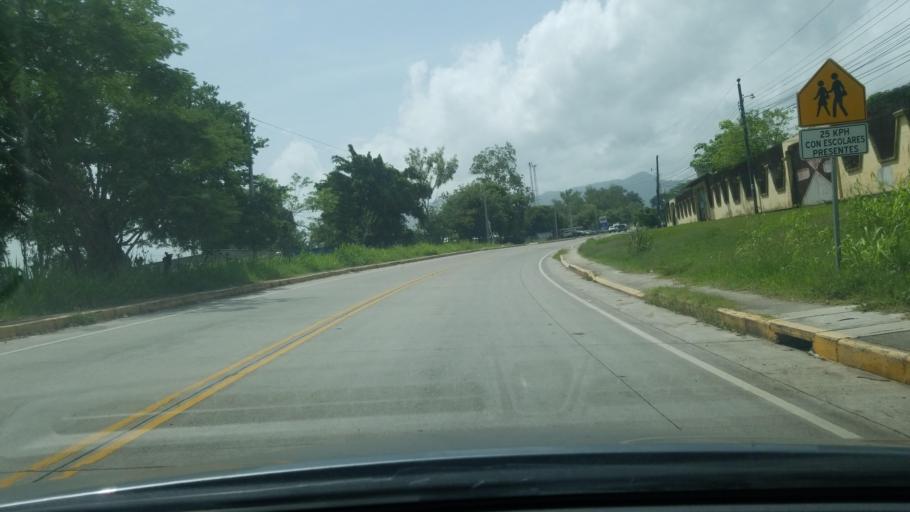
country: HN
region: Copan
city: La Entrada
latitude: 15.0699
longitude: -88.7648
